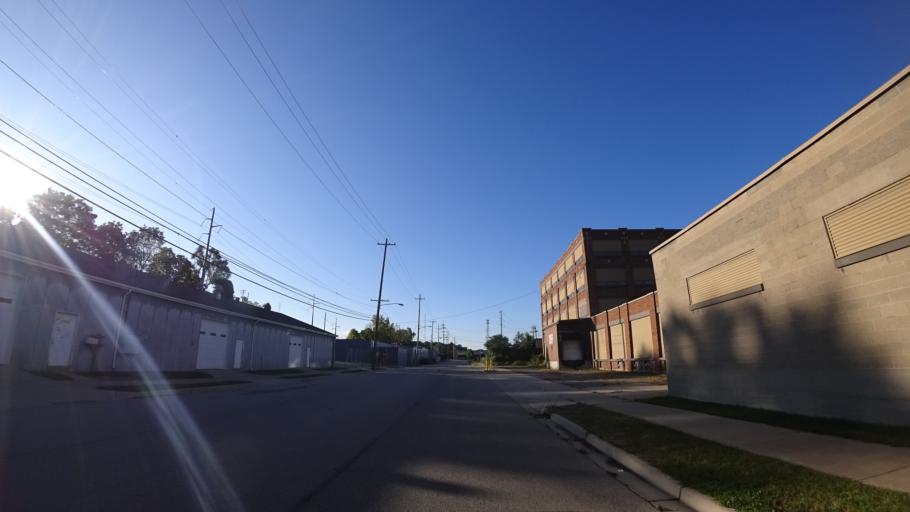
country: US
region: Michigan
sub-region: Kent County
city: Grand Rapids
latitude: 42.9873
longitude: -85.6687
